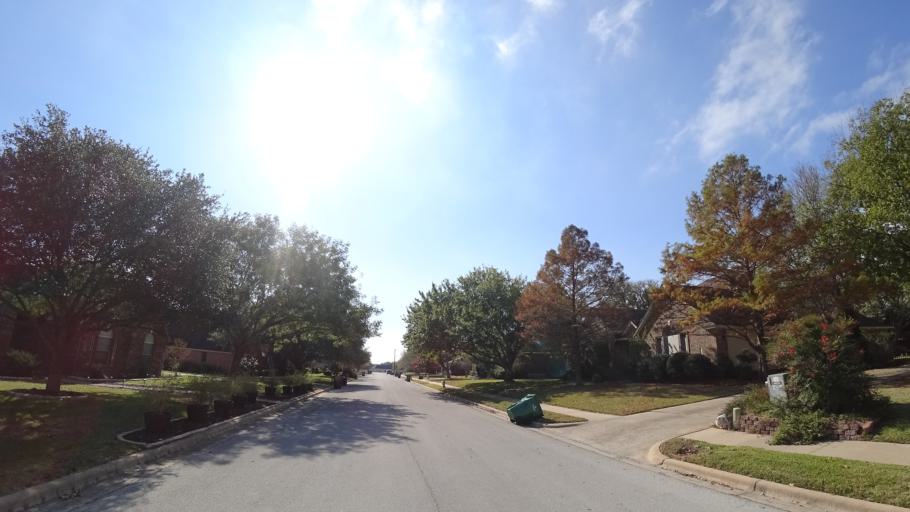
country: US
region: Texas
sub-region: Travis County
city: Shady Hollow
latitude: 30.1639
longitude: -97.8701
